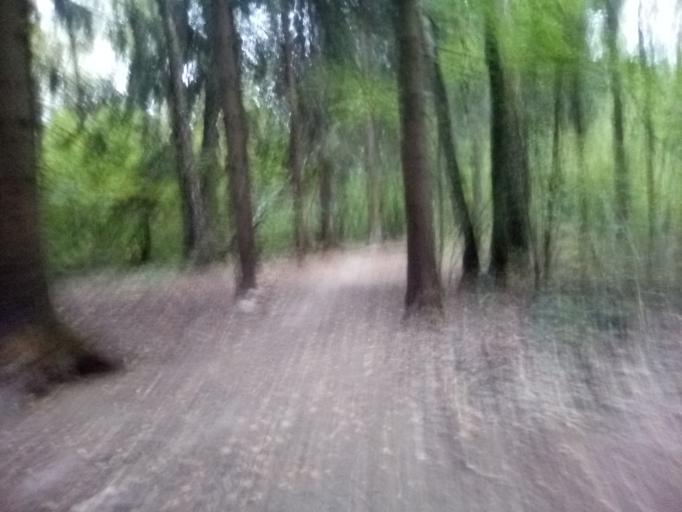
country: RU
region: Moscow
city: Novo-Peredelkino
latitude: 55.6209
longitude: 37.3279
